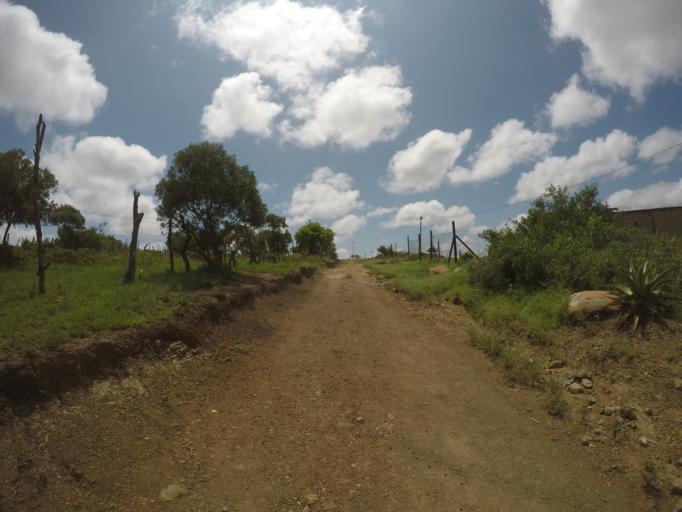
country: ZA
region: KwaZulu-Natal
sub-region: uThungulu District Municipality
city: Empangeni
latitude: -28.5781
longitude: 31.8383
